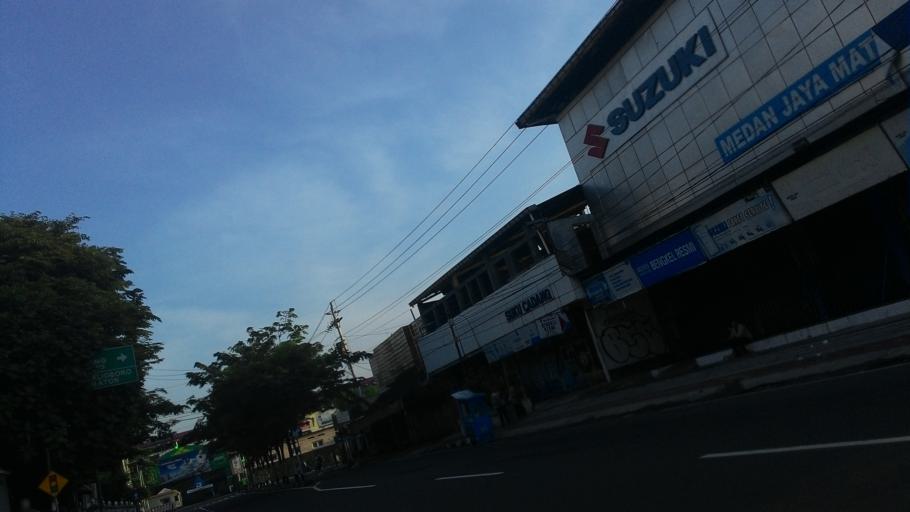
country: ID
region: Daerah Istimewa Yogyakarta
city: Yogyakarta
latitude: -7.7914
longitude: 110.3676
